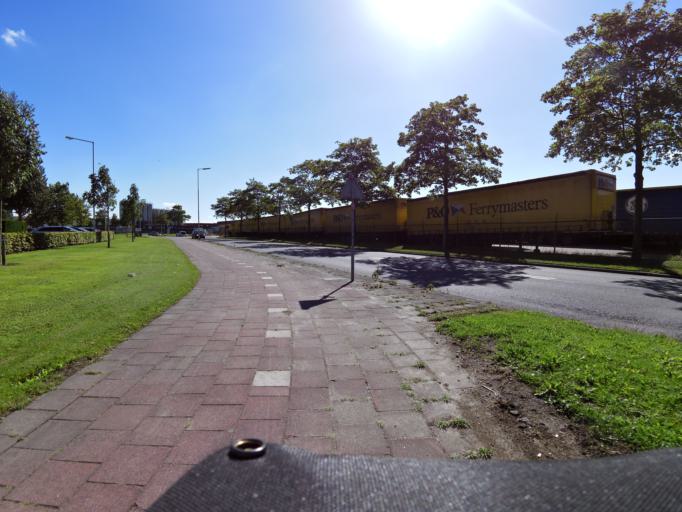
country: NL
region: South Holland
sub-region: Gemeente Spijkenisse
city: Spijkenisse
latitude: 51.8571
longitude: 4.2926
